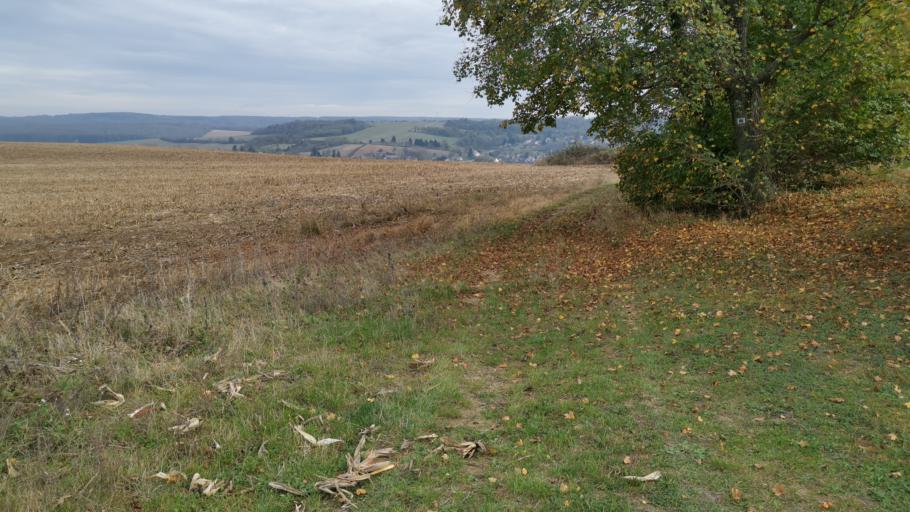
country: HU
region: Somogy
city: Kaposmero
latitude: 46.2748
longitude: 17.7187
